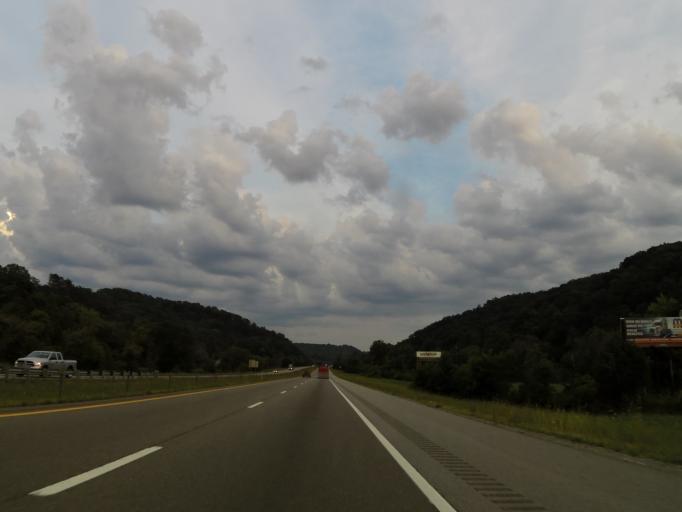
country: US
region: Tennessee
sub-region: Anderson County
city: Norris
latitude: 36.1492
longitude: -84.0621
